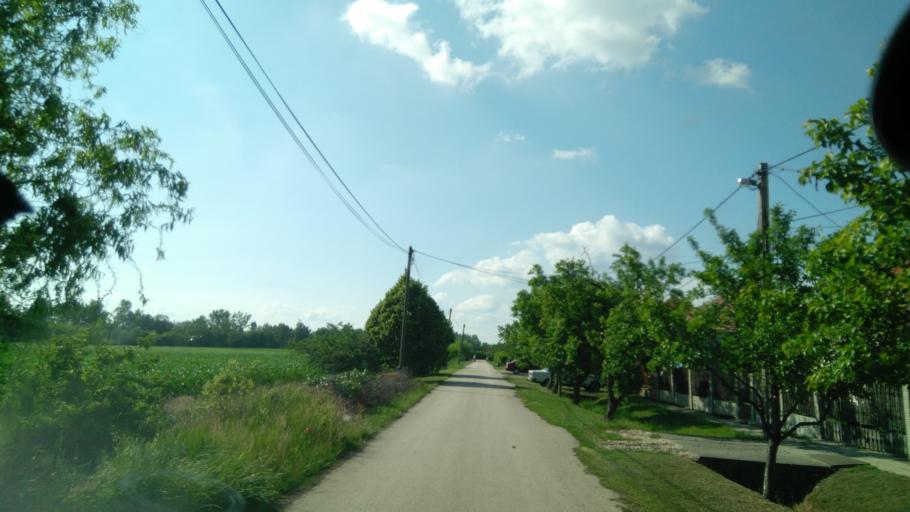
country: HU
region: Bekes
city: Bekes
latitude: 46.7030
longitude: 21.1772
